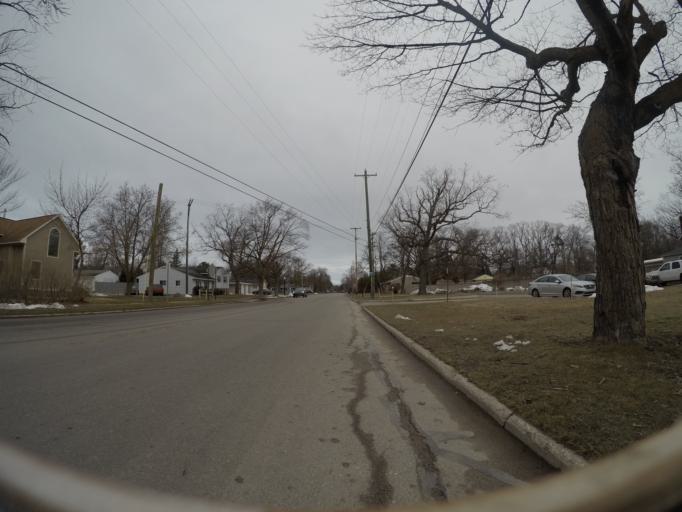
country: US
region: Michigan
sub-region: Grand Traverse County
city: Traverse City
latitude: 44.7595
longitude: -85.6003
